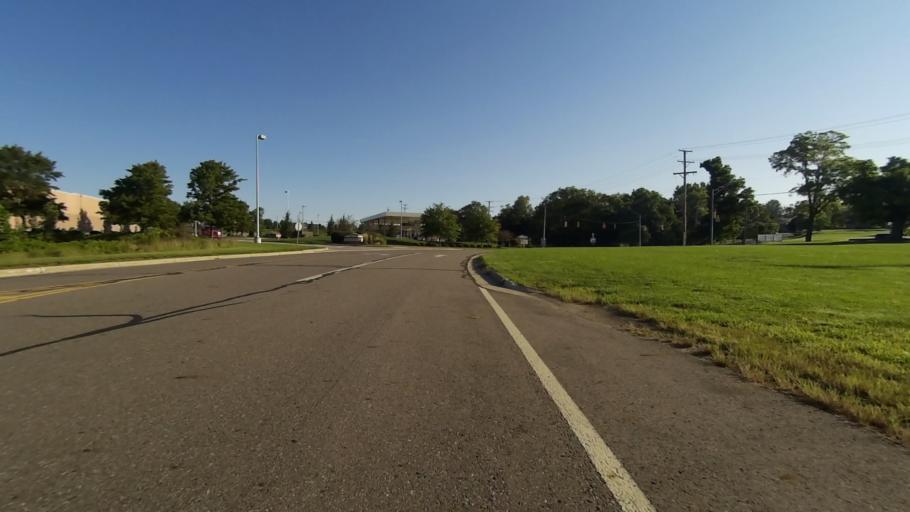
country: US
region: Ohio
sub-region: Portage County
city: Streetsboro
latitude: 41.2364
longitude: -81.3463
